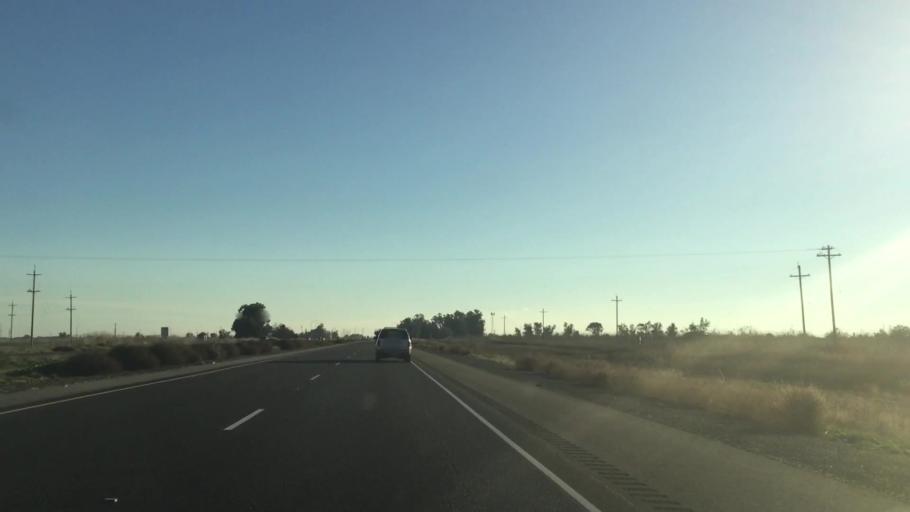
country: US
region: California
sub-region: Yuba County
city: Plumas Lake
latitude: 38.8746
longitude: -121.5436
